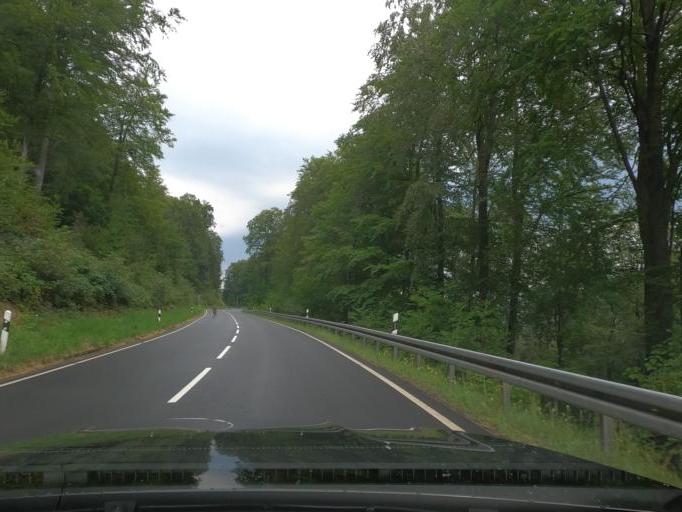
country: DE
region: Lower Saxony
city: Goslar
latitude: 51.8692
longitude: 10.3870
